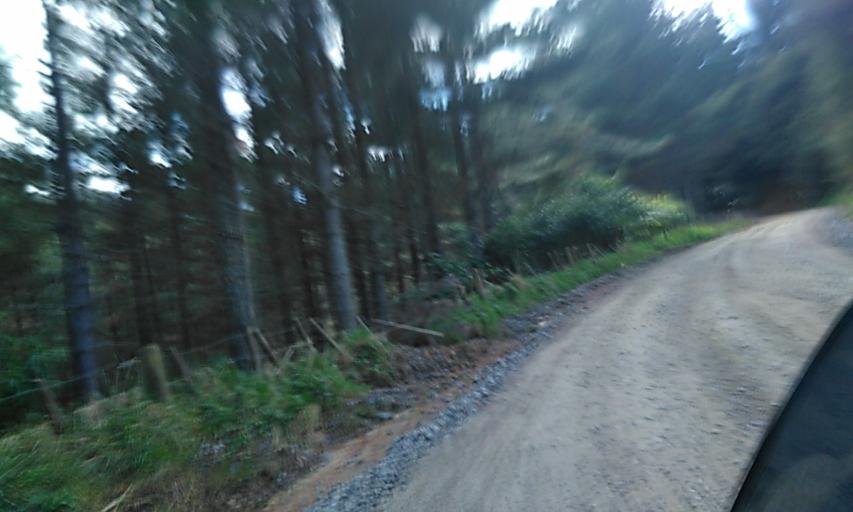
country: NZ
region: Gisborne
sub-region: Gisborne District
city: Gisborne
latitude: -38.3251
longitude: 178.0729
